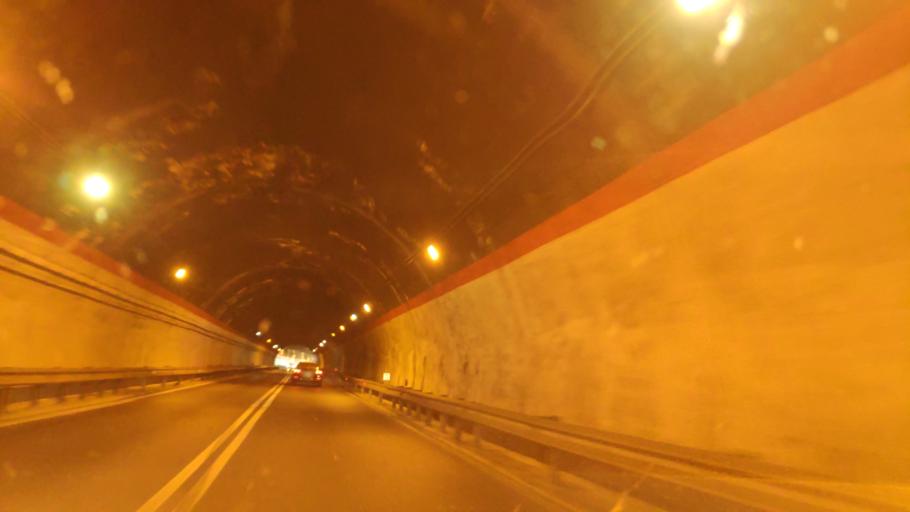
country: IT
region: Calabria
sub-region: Provincia di Catanzaro
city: Squillace Lido
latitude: 38.7639
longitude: 16.5673
